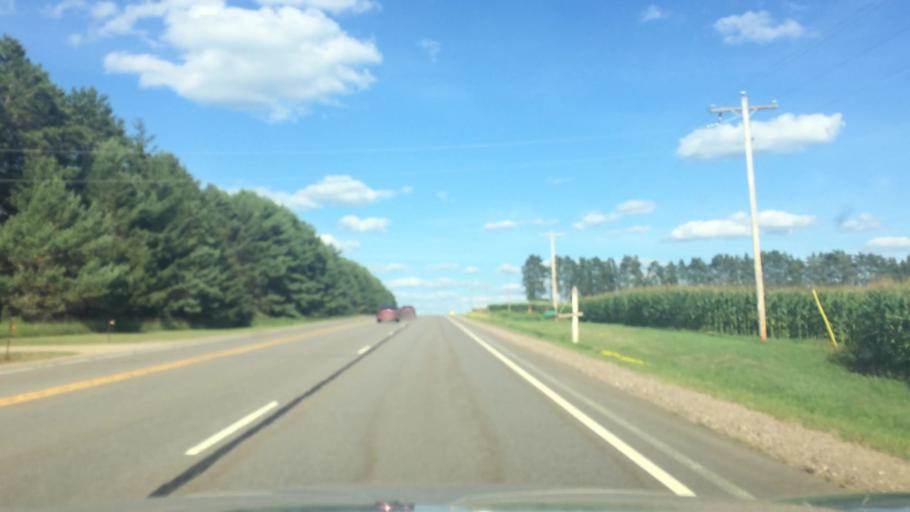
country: US
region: Wisconsin
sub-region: Lincoln County
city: Merrill
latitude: 45.1779
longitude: -89.6168
